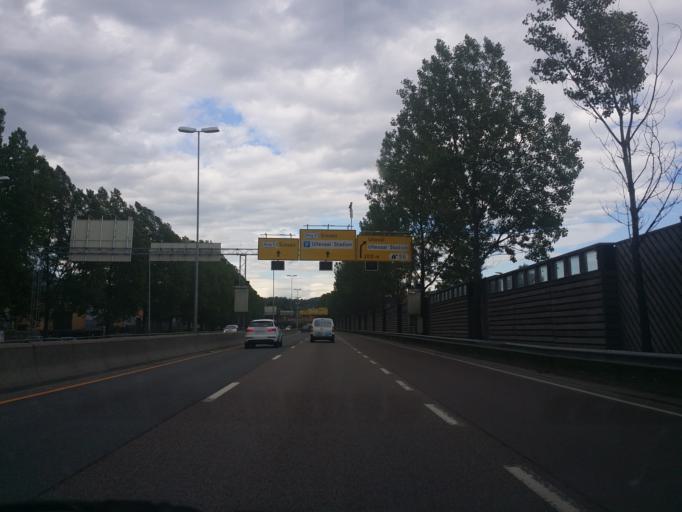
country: NO
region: Oslo
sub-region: Oslo
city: Oslo
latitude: 59.9481
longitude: 10.7255
